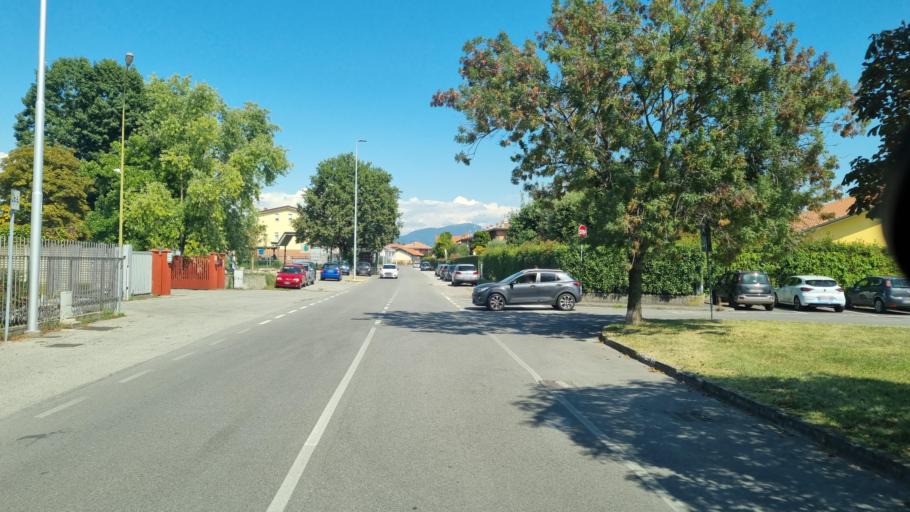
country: IT
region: Lombardy
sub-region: Provincia di Bergamo
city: Azzano San Paolo
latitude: 45.6589
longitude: 9.6660
